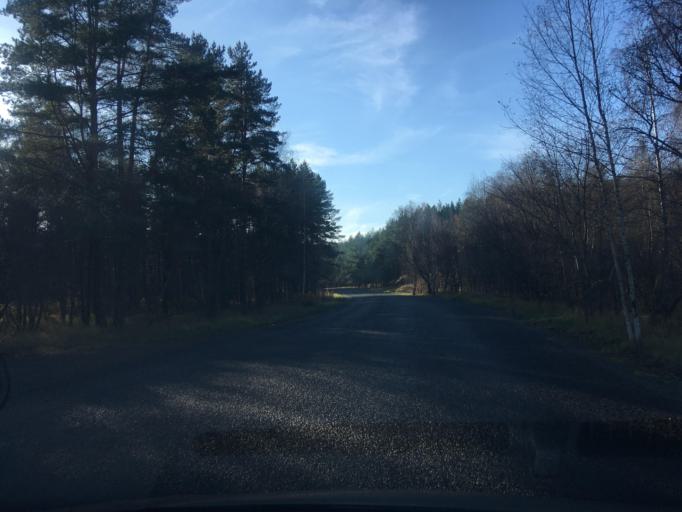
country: EE
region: Harju
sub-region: Maardu linn
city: Maardu
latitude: 59.4723
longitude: 25.0304
